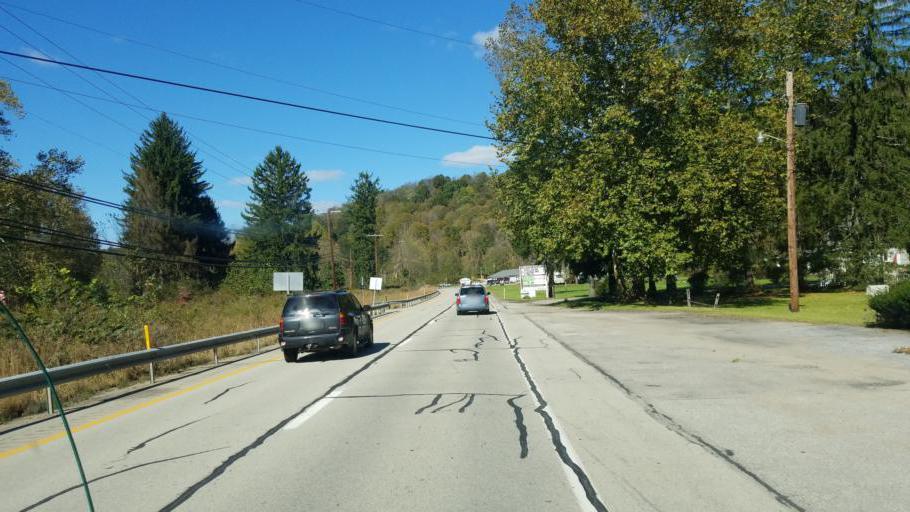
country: US
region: Pennsylvania
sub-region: Westmoreland County
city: Ligonier
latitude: 40.2573
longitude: -79.2629
